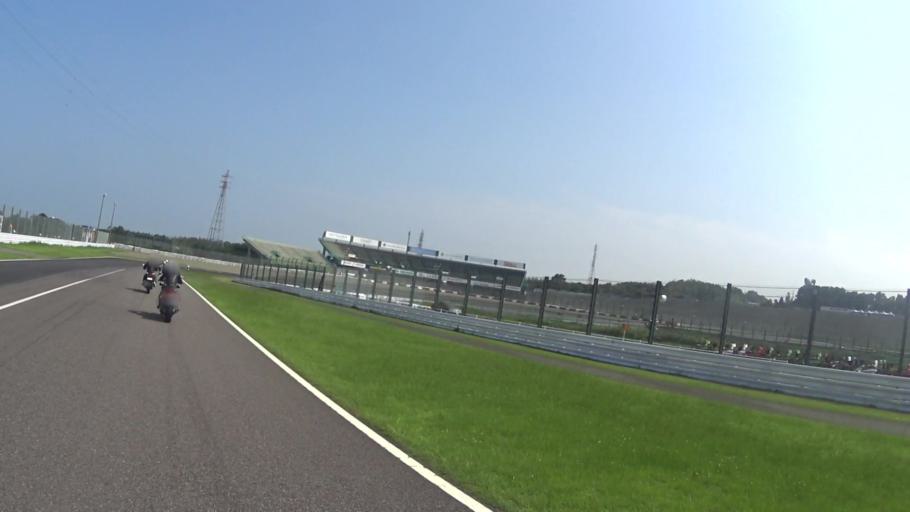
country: JP
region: Mie
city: Kawage
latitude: 34.8412
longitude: 136.5424
